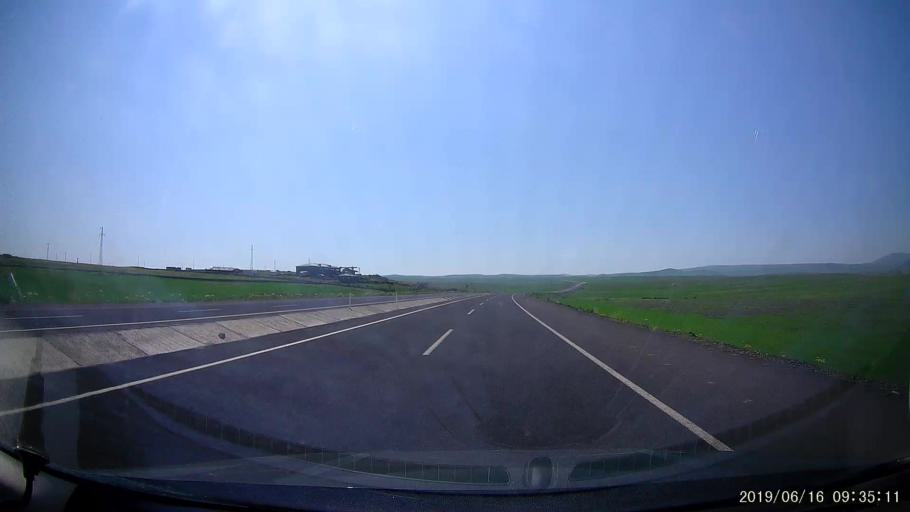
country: TR
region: Kars
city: Kars
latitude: 40.5754
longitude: 43.1516
